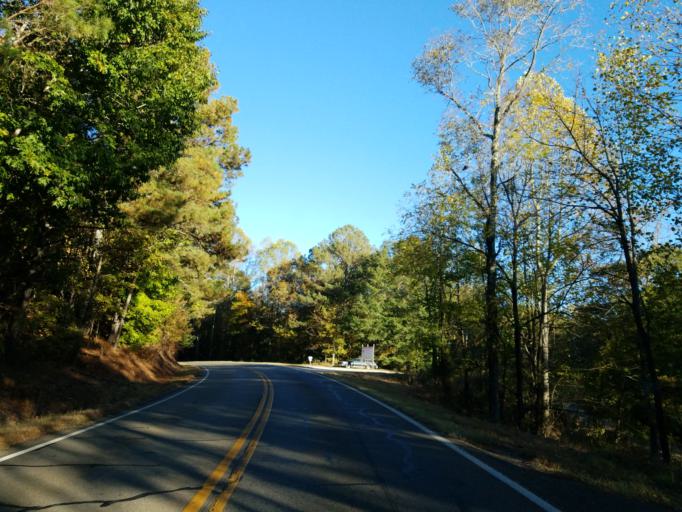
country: US
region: Georgia
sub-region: Pickens County
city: Nelson
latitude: 34.4153
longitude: -84.2604
